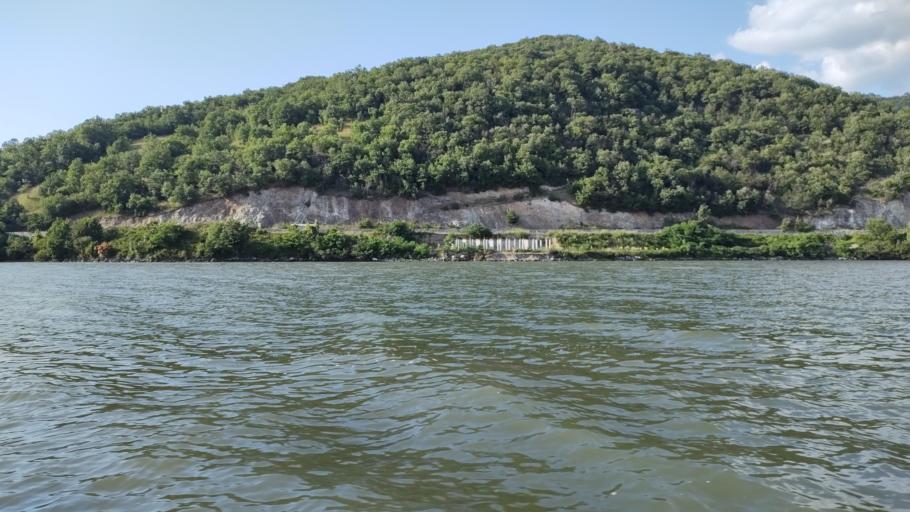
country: RO
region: Mehedinti
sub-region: Comuna Svinita
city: Svinita
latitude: 44.4799
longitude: 22.1655
